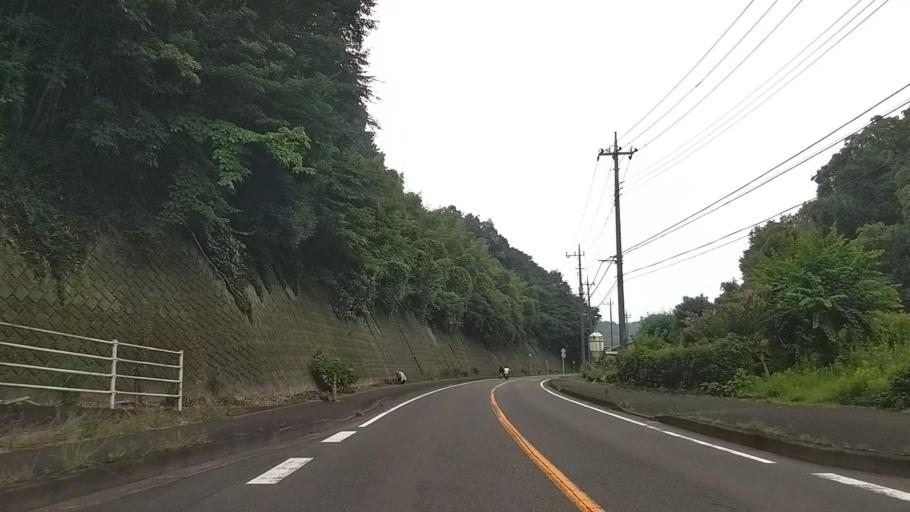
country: JP
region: Kanagawa
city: Hadano
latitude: 35.3340
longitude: 139.2200
